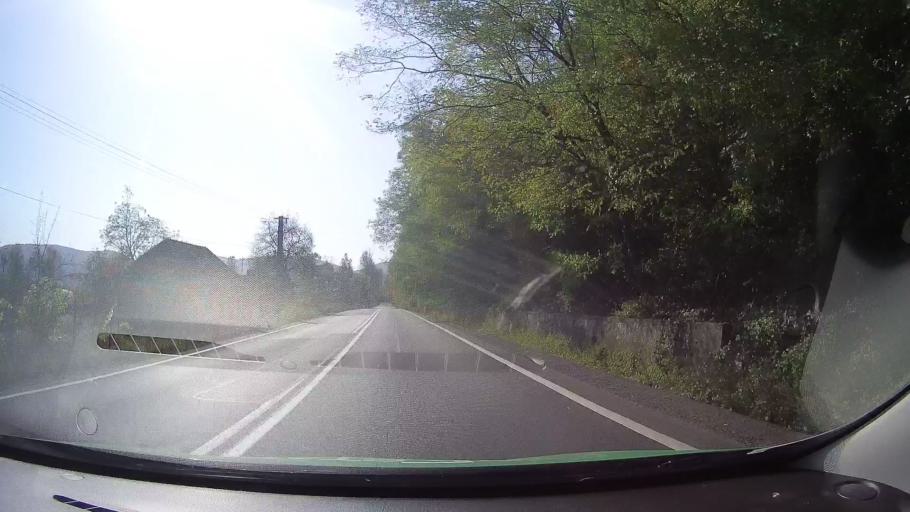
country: RO
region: Arad
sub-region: Comuna Petris
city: Petris
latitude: 46.0134
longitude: 22.3463
